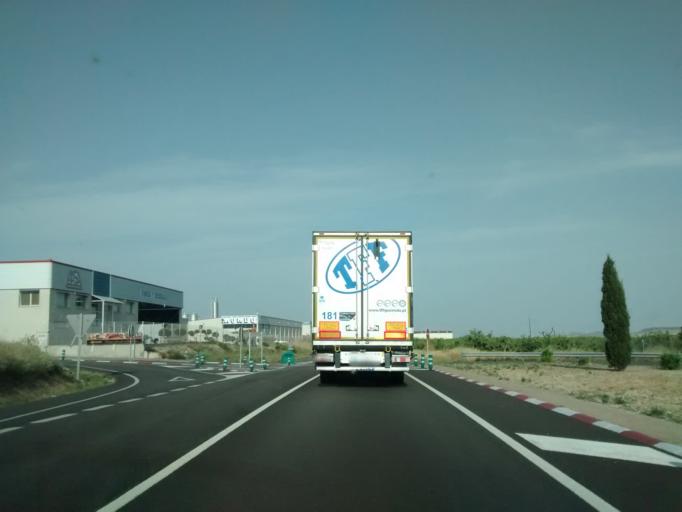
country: ES
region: Aragon
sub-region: Provincia de Zaragoza
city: Albeta
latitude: 41.8313
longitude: -1.5122
